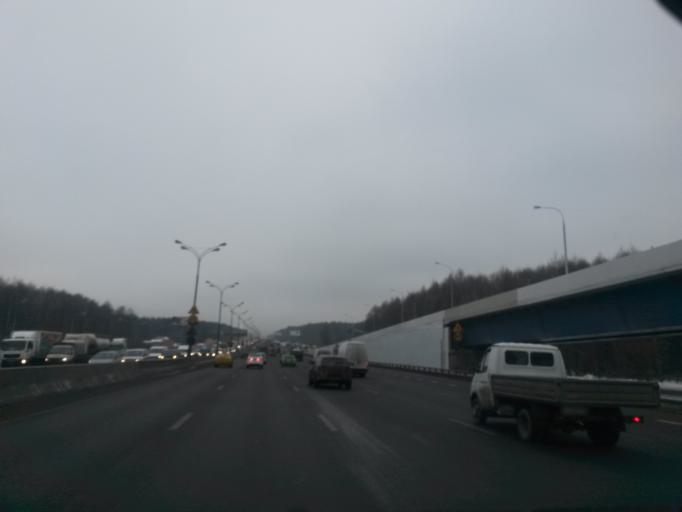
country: RU
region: Moskovskaya
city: Mosrentgen
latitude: 55.6420
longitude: 37.4562
